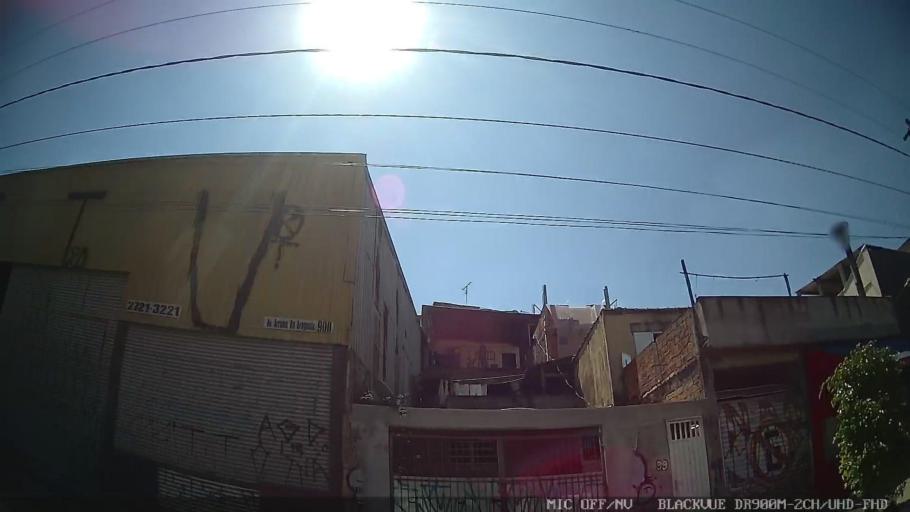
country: BR
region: Sao Paulo
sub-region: Sao Caetano Do Sul
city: Sao Caetano do Sul
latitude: -23.5819
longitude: -46.5035
